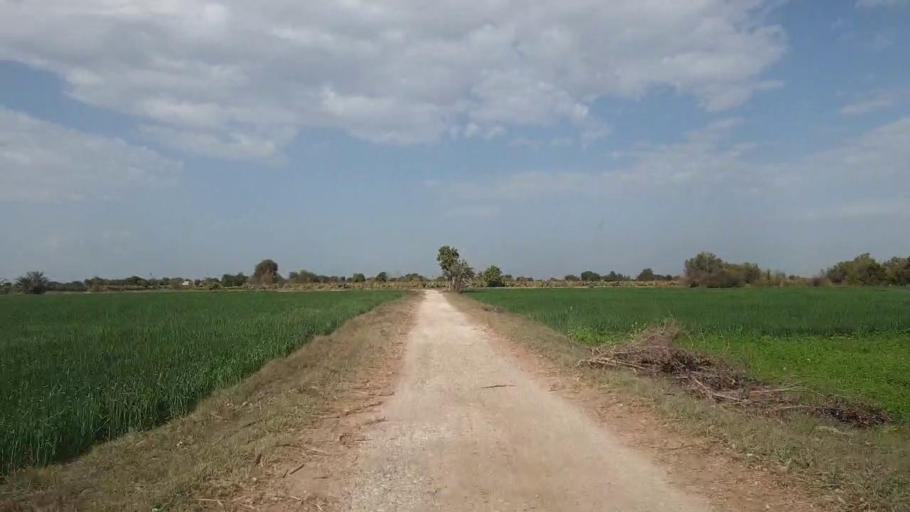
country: PK
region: Sindh
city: Shahdadpur
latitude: 25.9852
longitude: 68.4787
